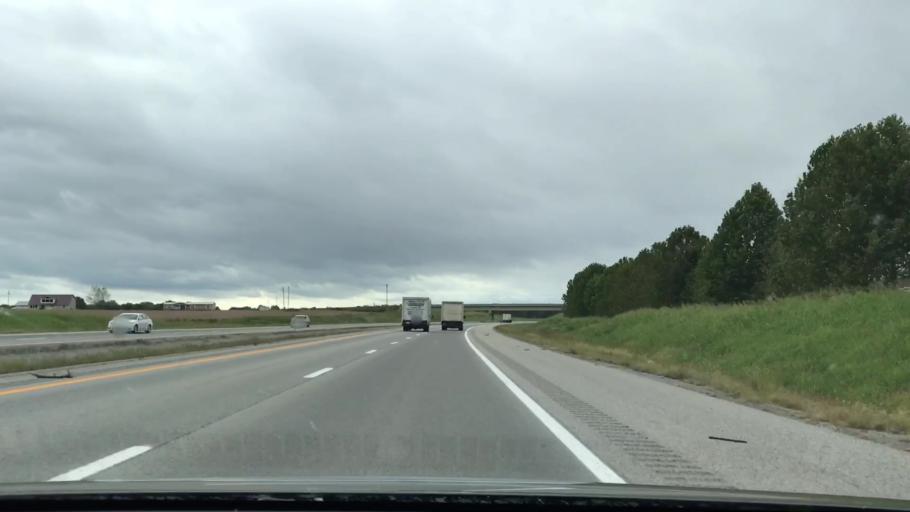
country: US
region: Kentucky
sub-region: Christian County
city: Hopkinsville
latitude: 36.7670
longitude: -87.4998
